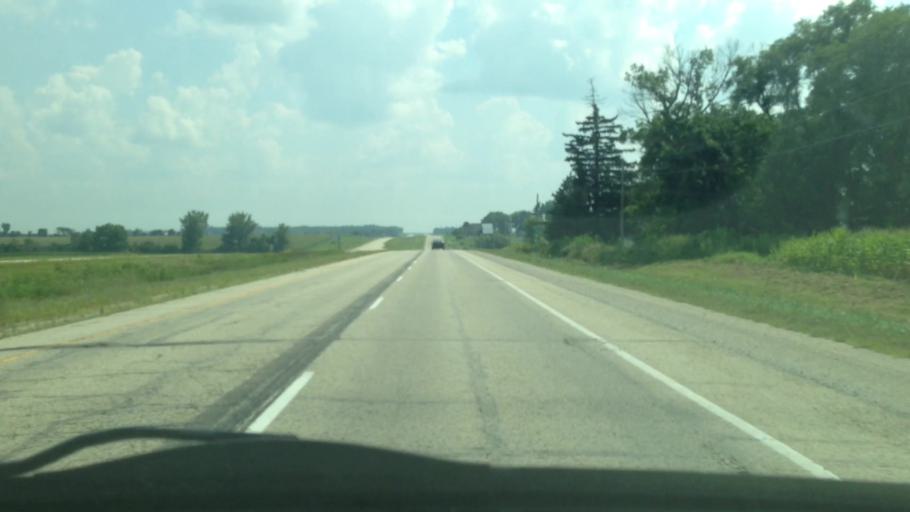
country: US
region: Iowa
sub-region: Chickasaw County
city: New Hampton
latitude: 42.9551
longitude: -92.3177
